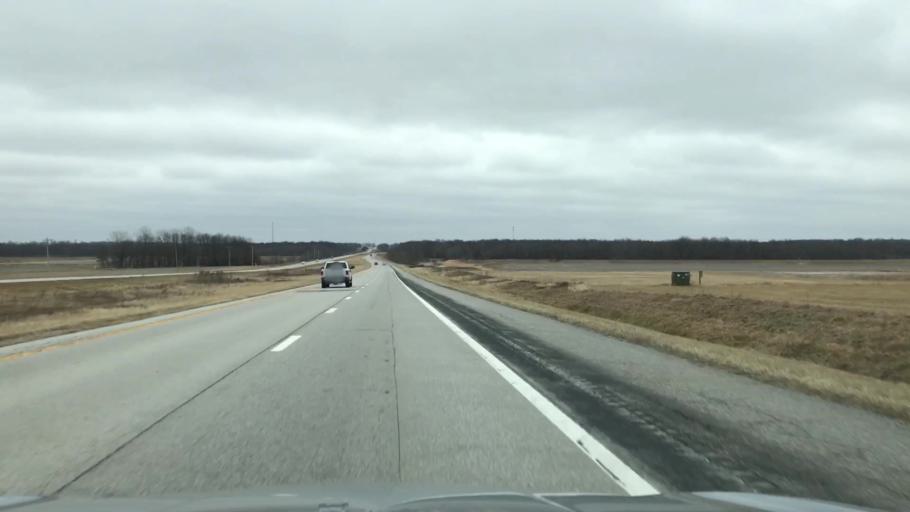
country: US
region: Missouri
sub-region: Linn County
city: Linneus
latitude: 39.7774
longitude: -93.3405
